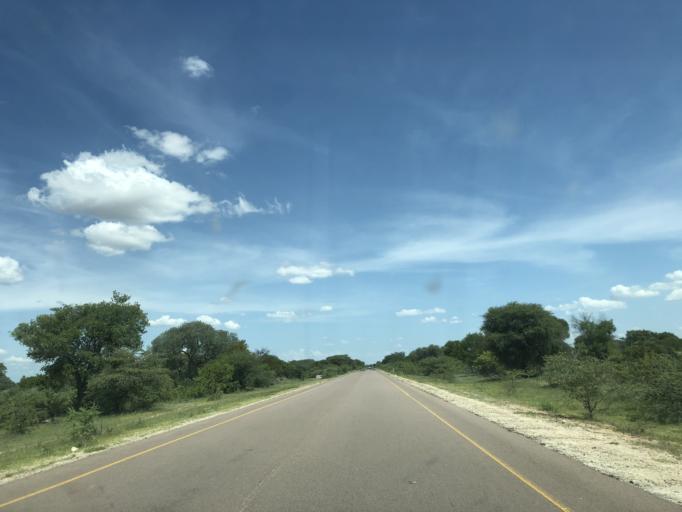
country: AO
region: Cunene
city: Ondjiva
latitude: -16.8651
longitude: 15.4767
